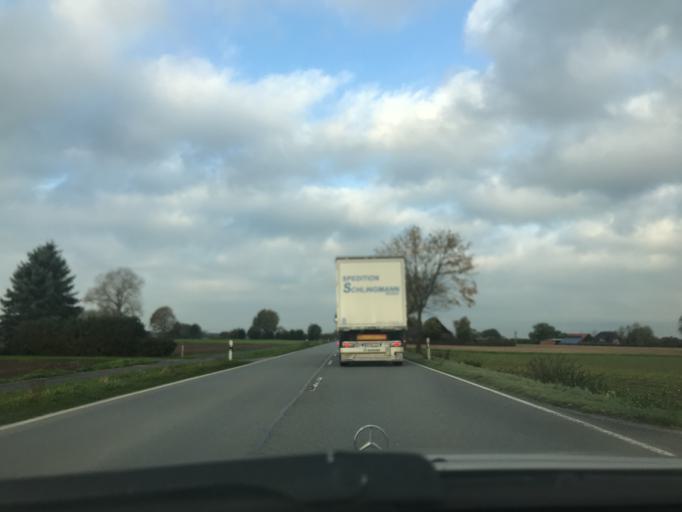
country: DE
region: North Rhine-Westphalia
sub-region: Regierungsbezirk Arnsberg
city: Soest
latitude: 51.6455
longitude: 8.0897
